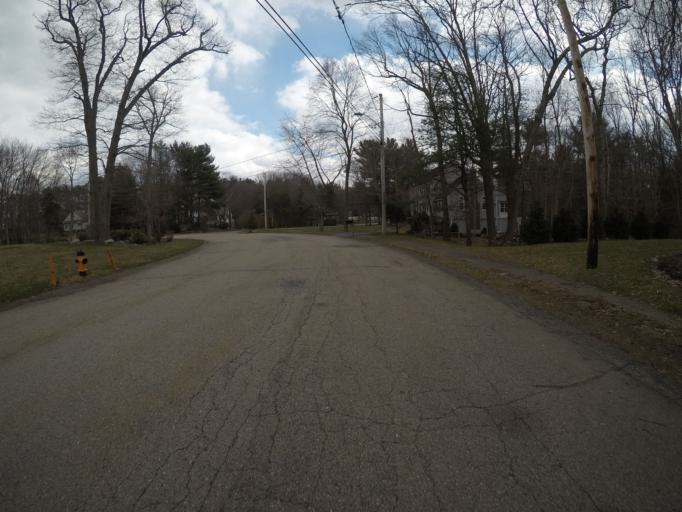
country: US
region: Massachusetts
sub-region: Bristol County
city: Easton
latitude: 42.0611
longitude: -71.1353
